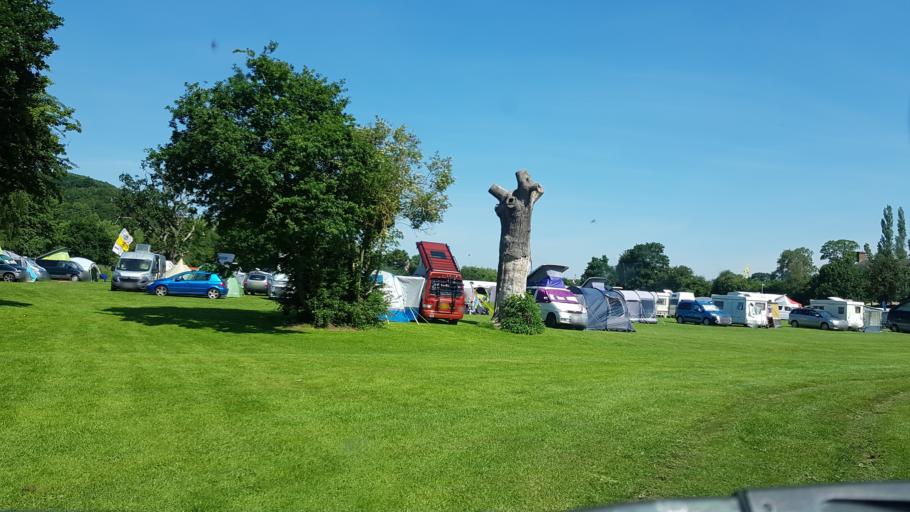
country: GB
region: England
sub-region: Worcestershire
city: Stourport-on-Severn
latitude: 52.3422
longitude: -2.3002
